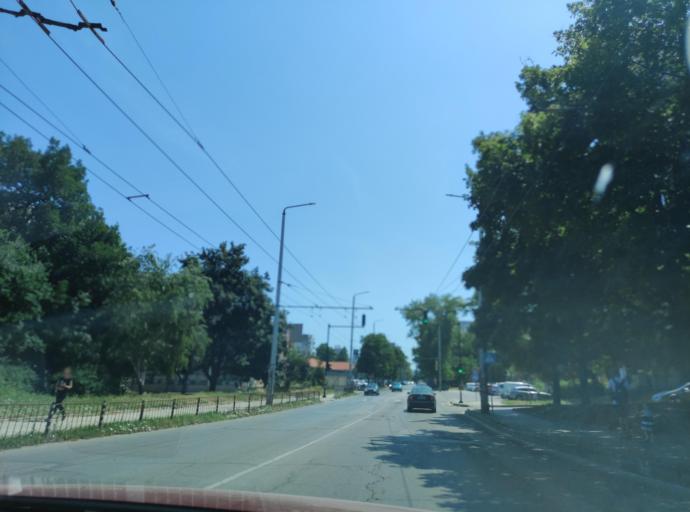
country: BG
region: Pleven
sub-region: Obshtina Pleven
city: Pleven
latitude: 43.4240
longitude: 24.5935
